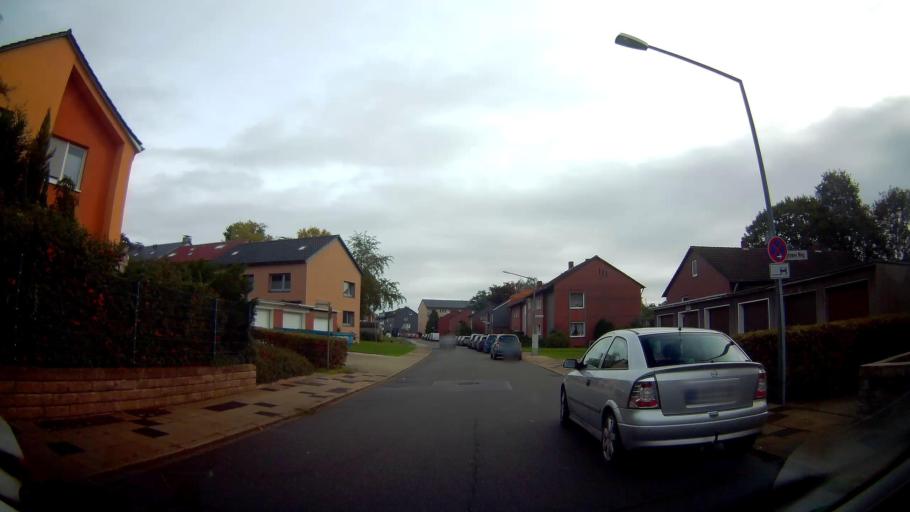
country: DE
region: North Rhine-Westphalia
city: Herten
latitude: 51.5979
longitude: 7.1332
